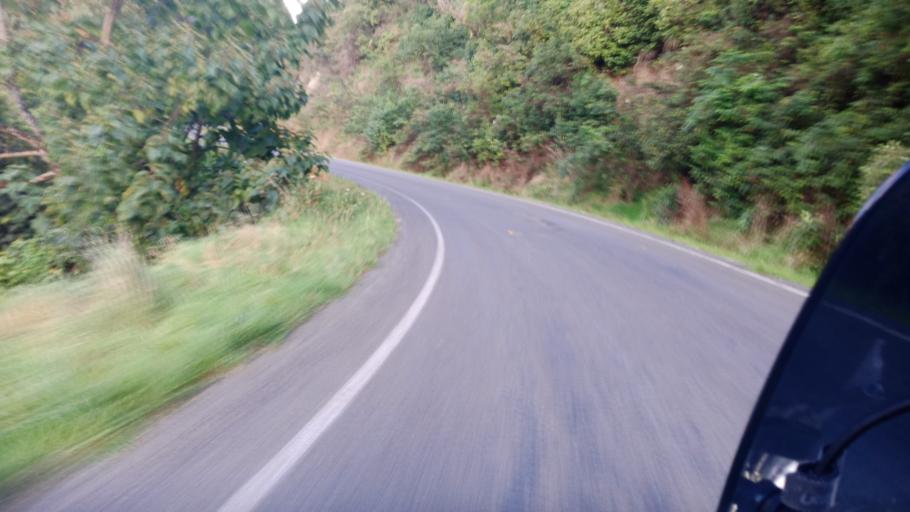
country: NZ
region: Gisborne
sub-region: Gisborne District
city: Gisborne
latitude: -38.5299
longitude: 177.5426
